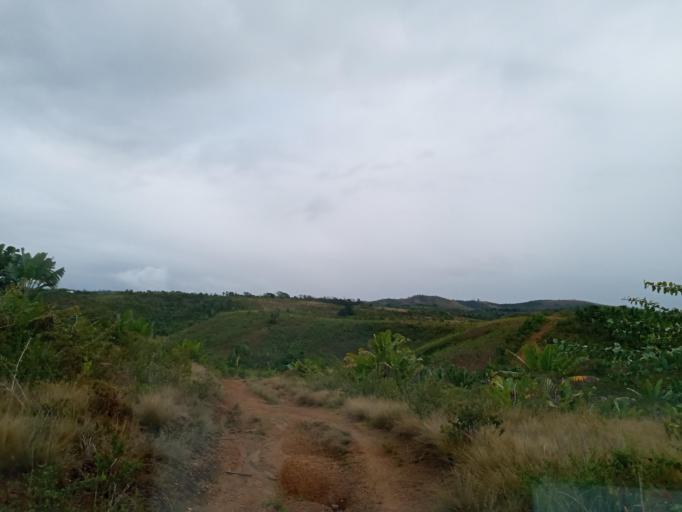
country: MG
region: Atsimo-Atsinanana
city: Vohipaho
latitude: -24.0067
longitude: 47.4114
